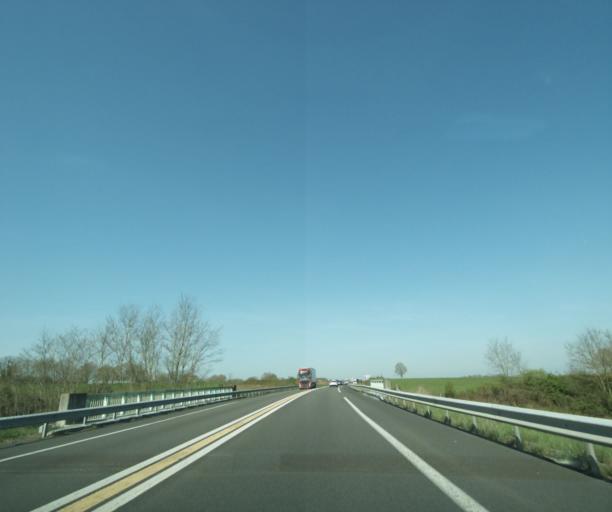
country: FR
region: Auvergne
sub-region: Departement de l'Allier
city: Diou
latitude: 46.5174
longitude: 3.7411
